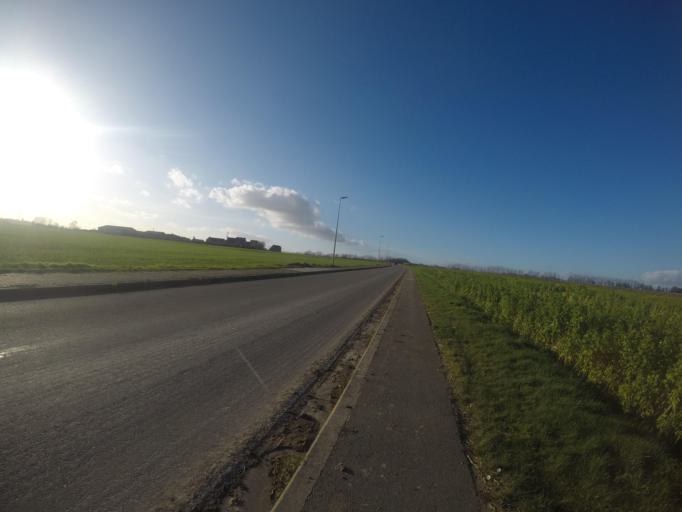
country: BE
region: Wallonia
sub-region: Province du Brabant Wallon
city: Tubize
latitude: 50.6960
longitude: 4.1767
